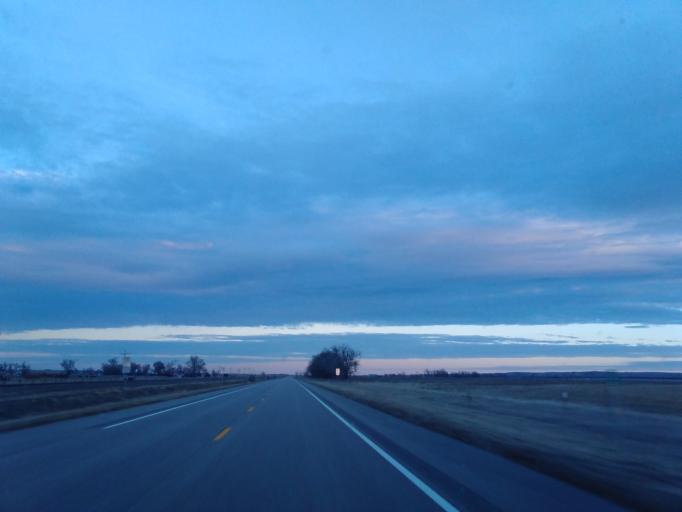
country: US
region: Nebraska
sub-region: Garden County
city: Oshkosh
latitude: 41.3944
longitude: -102.3104
